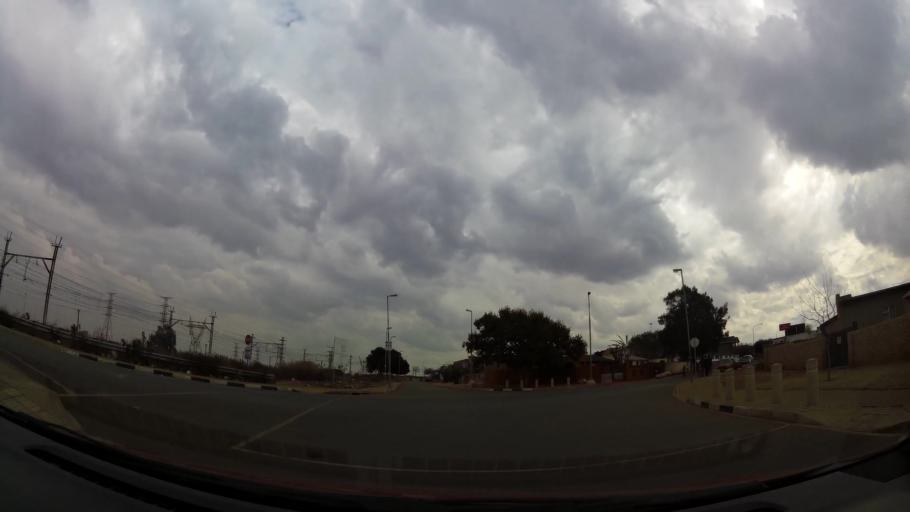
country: ZA
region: Gauteng
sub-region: City of Johannesburg Metropolitan Municipality
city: Soweto
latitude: -26.2650
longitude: 27.8325
